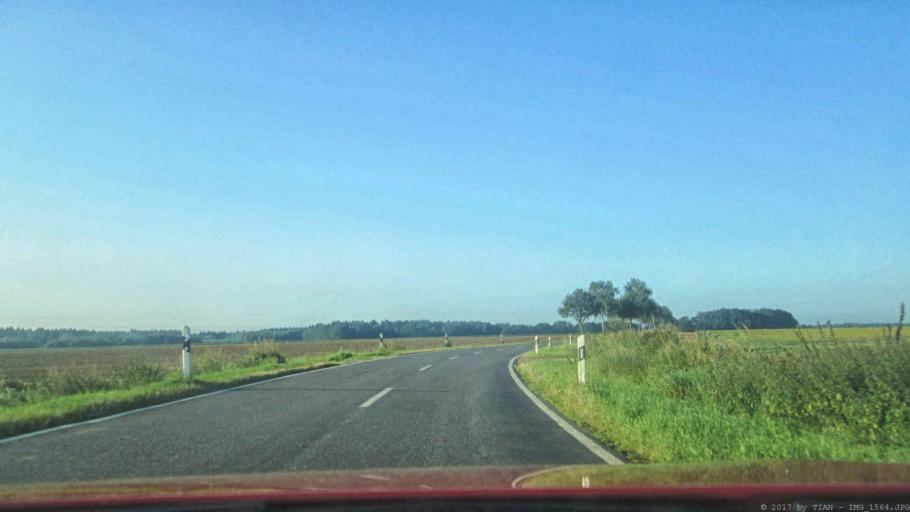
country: DE
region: Lower Saxony
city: Wittingen
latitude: 52.6831
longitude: 10.8062
